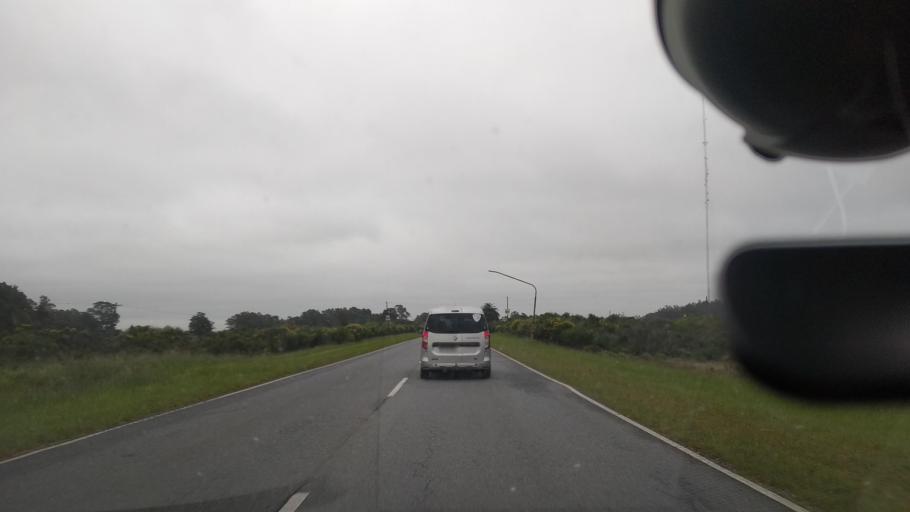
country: AR
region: Buenos Aires
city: Veronica
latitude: -35.4060
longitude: -57.3500
